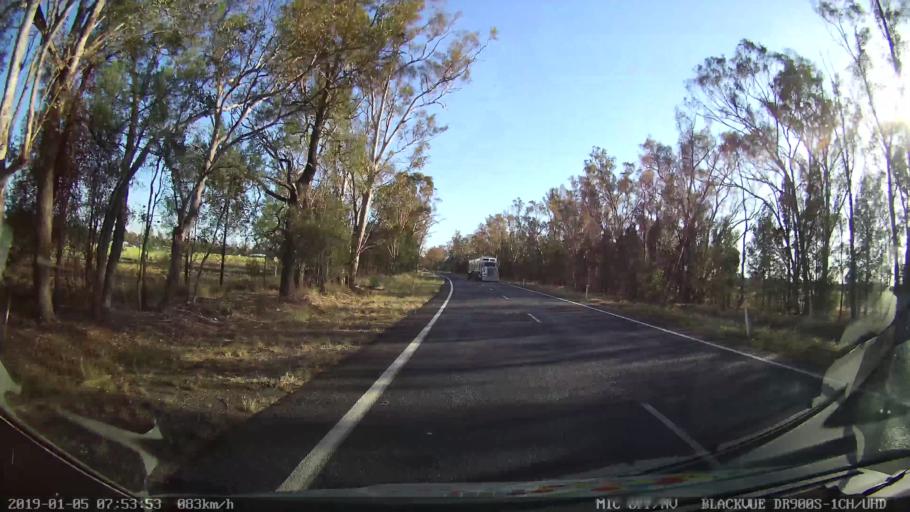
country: AU
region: New South Wales
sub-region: Gilgandra
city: Gilgandra
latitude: -31.7393
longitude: 148.6452
